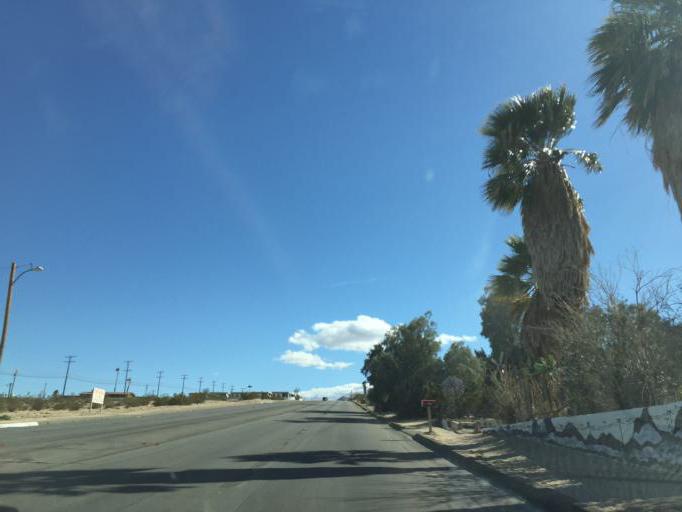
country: US
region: California
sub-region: San Bernardino County
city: Twentynine Palms
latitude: 34.1564
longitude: -116.0542
